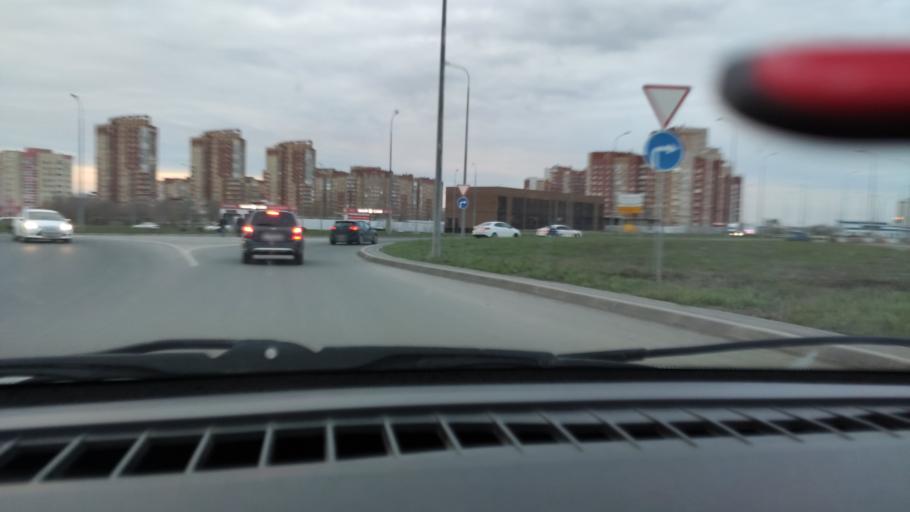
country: RU
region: Orenburg
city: Orenburg
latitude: 51.8221
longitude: 55.1595
